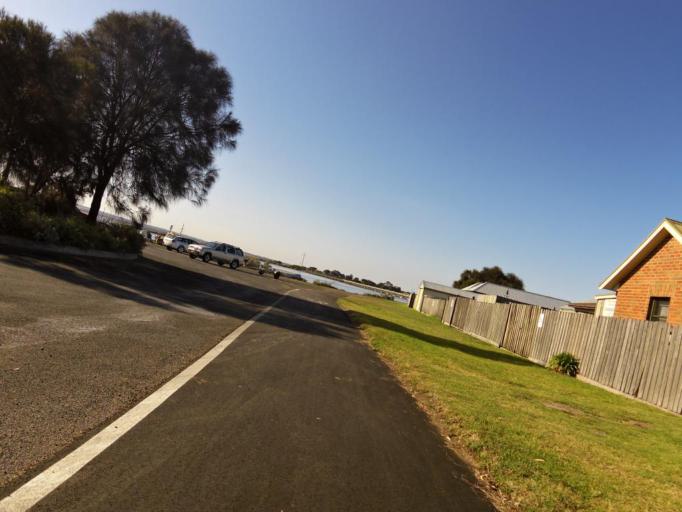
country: AU
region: Victoria
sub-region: Queenscliffe
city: Queenscliff
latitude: -38.2638
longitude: 144.6645
